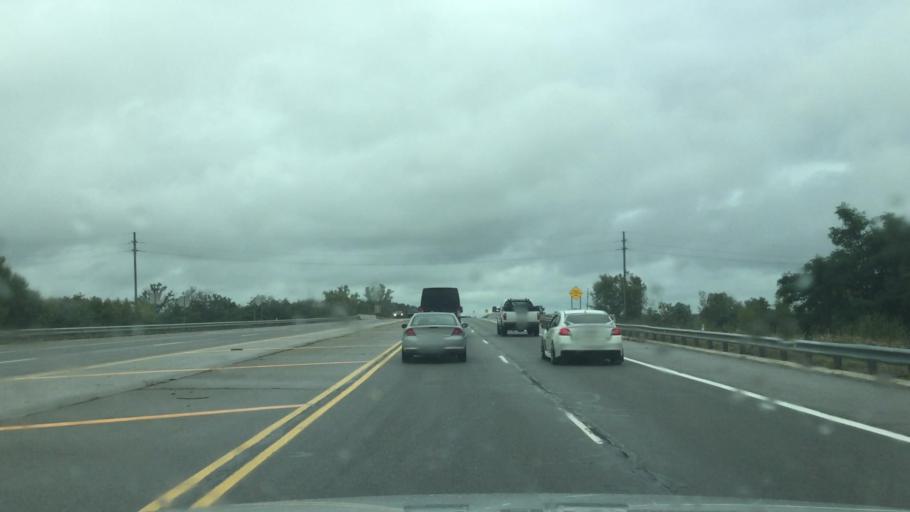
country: US
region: Michigan
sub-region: Livingston County
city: Howell
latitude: 42.6189
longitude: -83.9890
